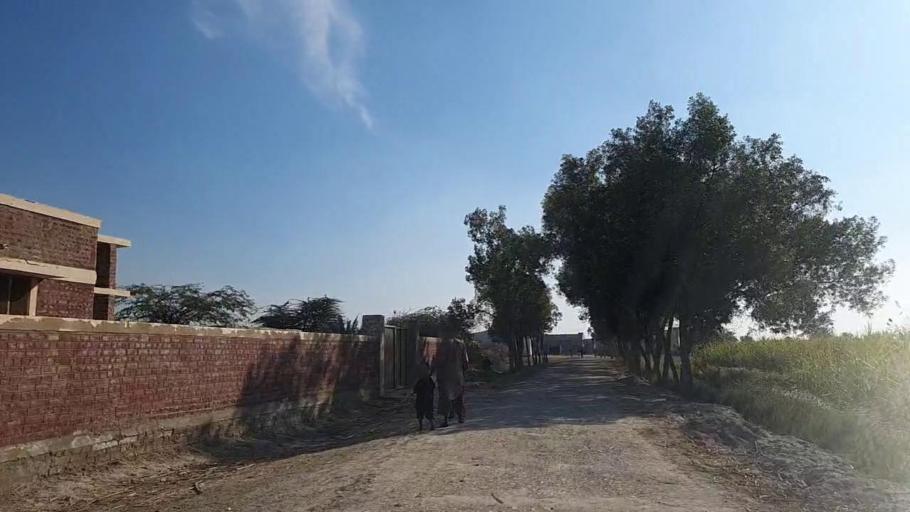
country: PK
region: Sindh
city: Bandhi
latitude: 26.5497
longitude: 68.2988
